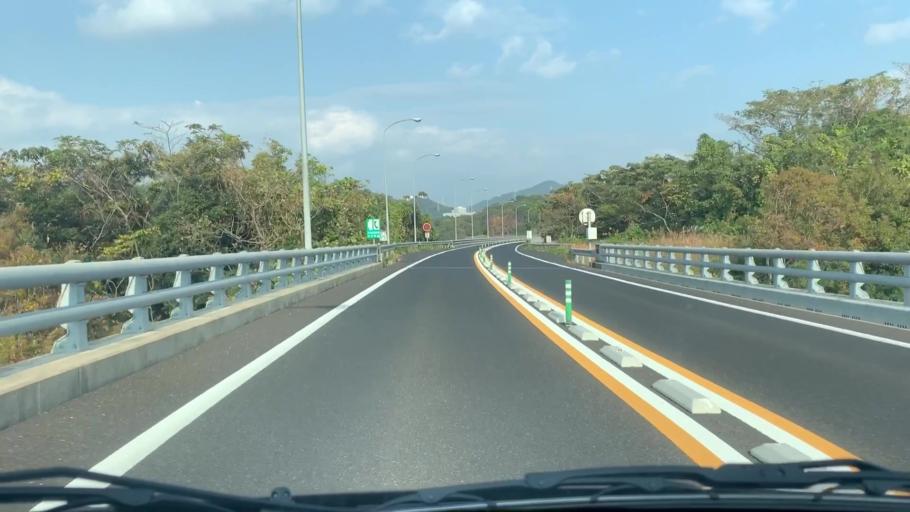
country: JP
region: Nagasaki
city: Sasebo
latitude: 33.0763
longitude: 129.7690
